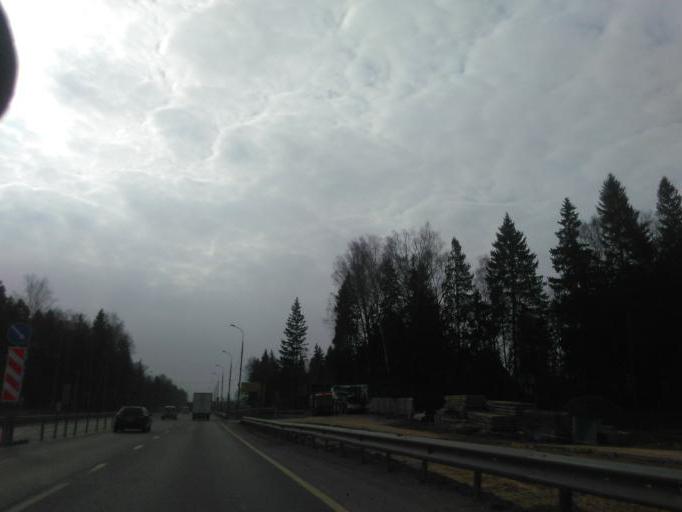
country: RU
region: Moskovskaya
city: Yermolino
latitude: 56.1368
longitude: 37.4980
